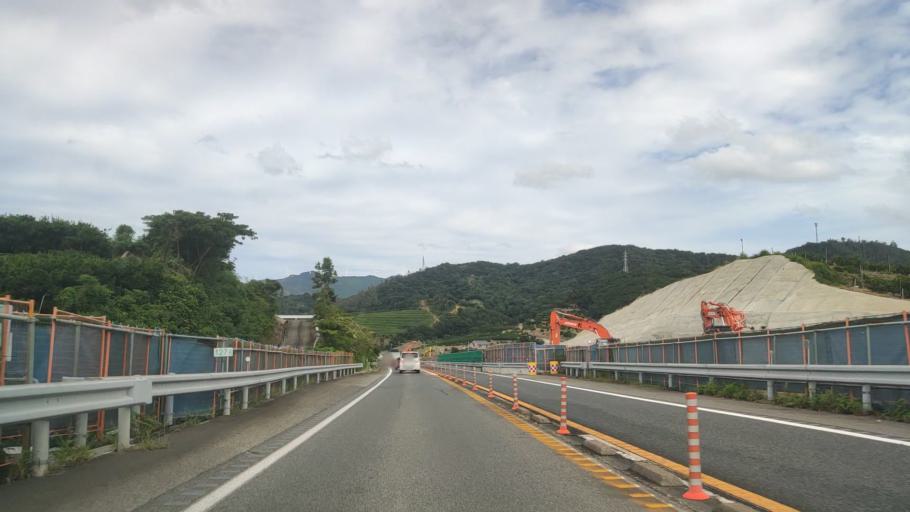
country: JP
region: Wakayama
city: Gobo
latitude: 33.9113
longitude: 135.1944
